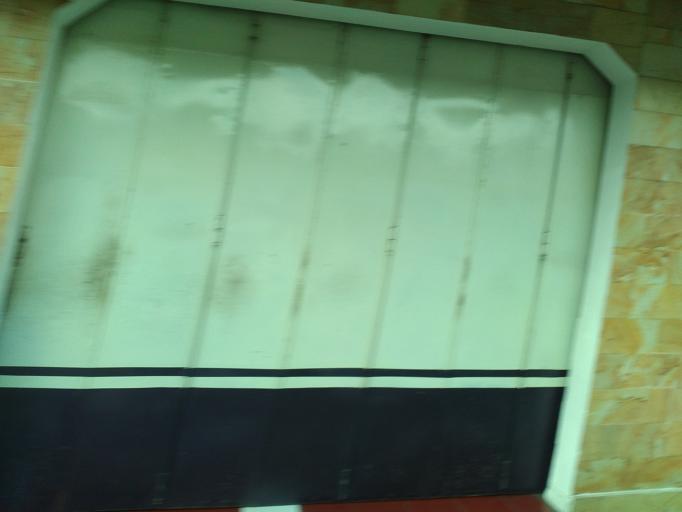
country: ID
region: Central Java
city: Ceper
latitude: -7.6772
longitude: 110.6492
